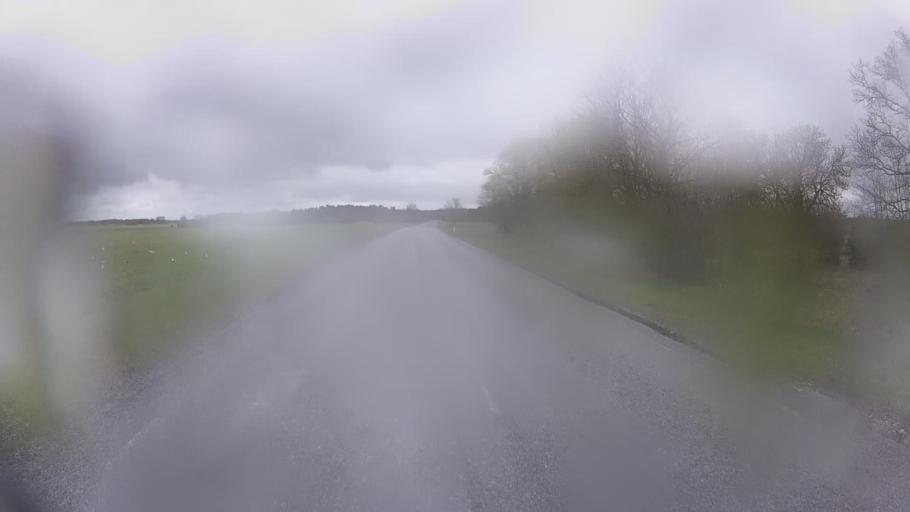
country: EE
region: Hiiumaa
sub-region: Kaerdla linn
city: Kardla
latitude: 58.8347
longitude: 22.8048
